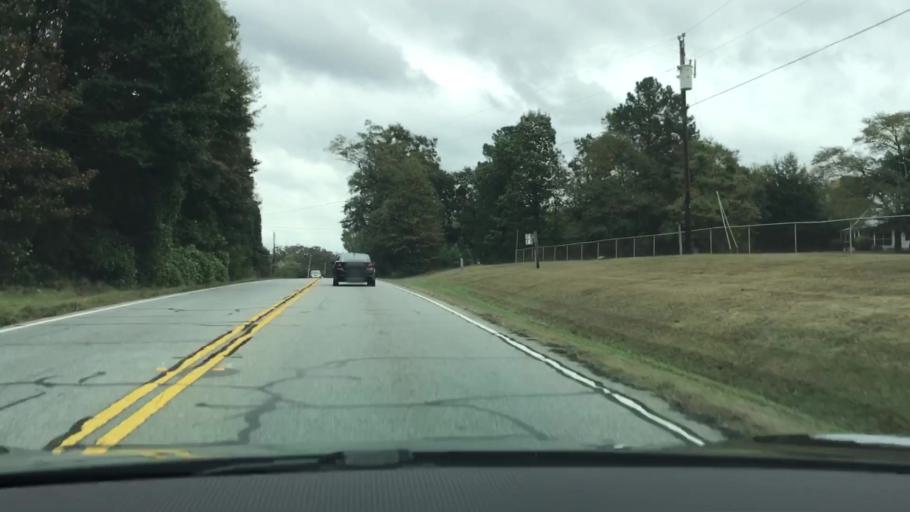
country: US
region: Georgia
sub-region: Oconee County
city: Watkinsville
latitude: 33.8715
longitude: -83.4323
